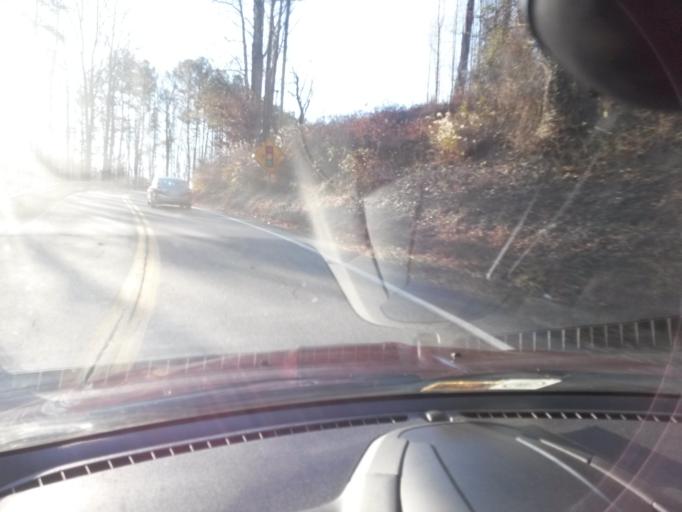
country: US
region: Virginia
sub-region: Patrick County
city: Stuart
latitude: 36.6419
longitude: -80.2642
